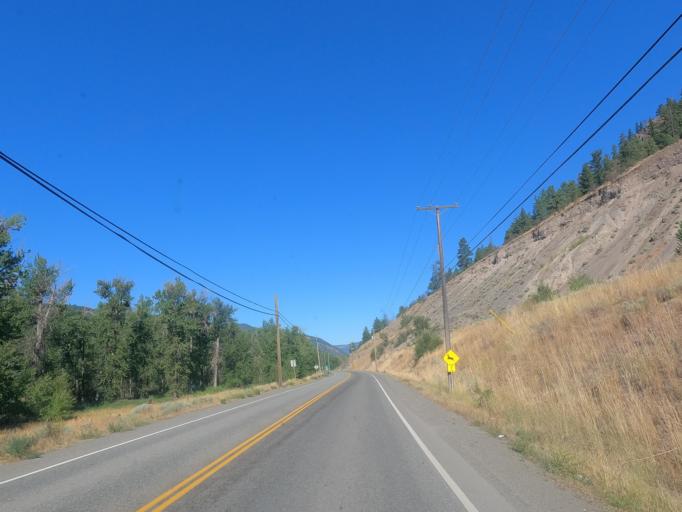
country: CA
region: British Columbia
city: Merritt
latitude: 50.1157
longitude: -120.8054
